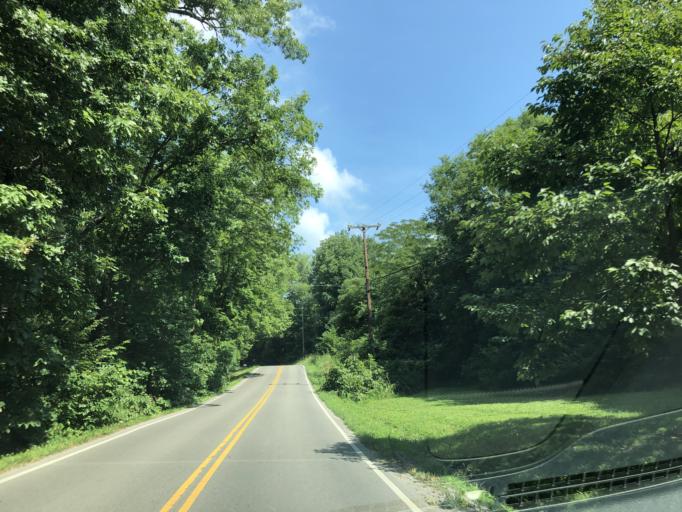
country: US
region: Tennessee
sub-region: Williamson County
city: Nolensville
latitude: 36.0125
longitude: -86.6720
